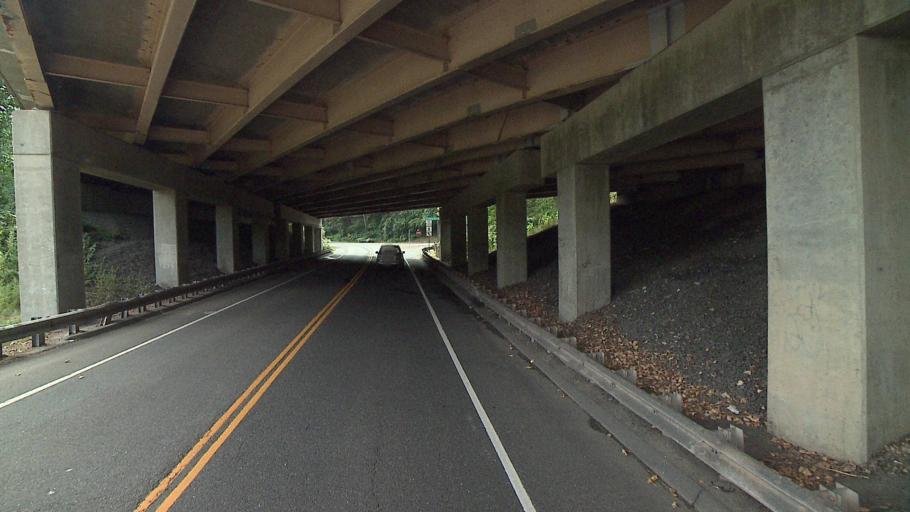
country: US
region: Connecticut
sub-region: New Haven County
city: Seymour
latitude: 41.3818
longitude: -73.0792
